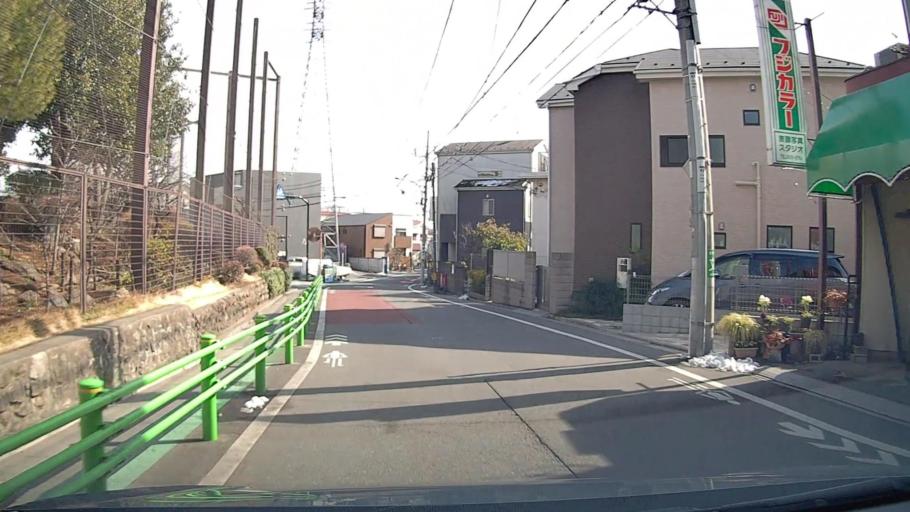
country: JP
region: Tokyo
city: Nishi-Tokyo-shi
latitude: 35.7441
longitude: 139.5727
